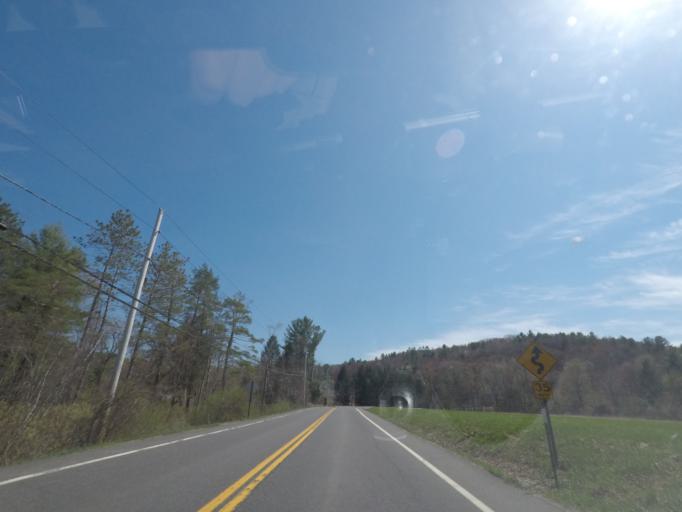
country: US
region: New York
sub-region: Rensselaer County
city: Nassau
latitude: 42.4717
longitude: -73.4753
